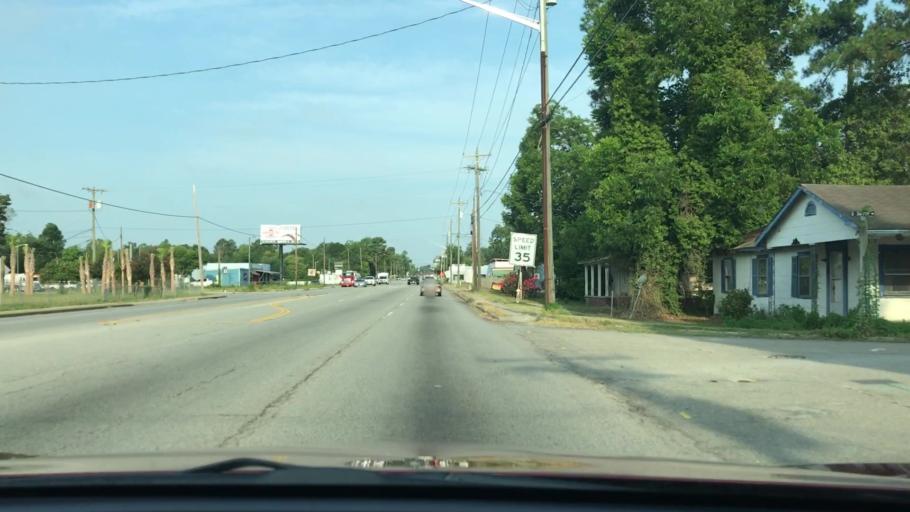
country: US
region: South Carolina
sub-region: Orangeburg County
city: Edisto
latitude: 33.4815
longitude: -80.8899
